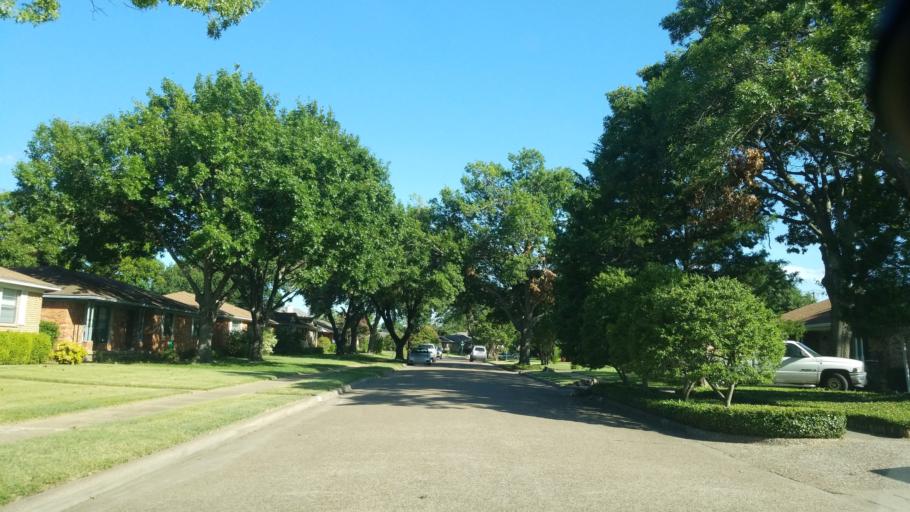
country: US
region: Texas
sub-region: Dallas County
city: Balch Springs
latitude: 32.7904
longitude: -96.7016
